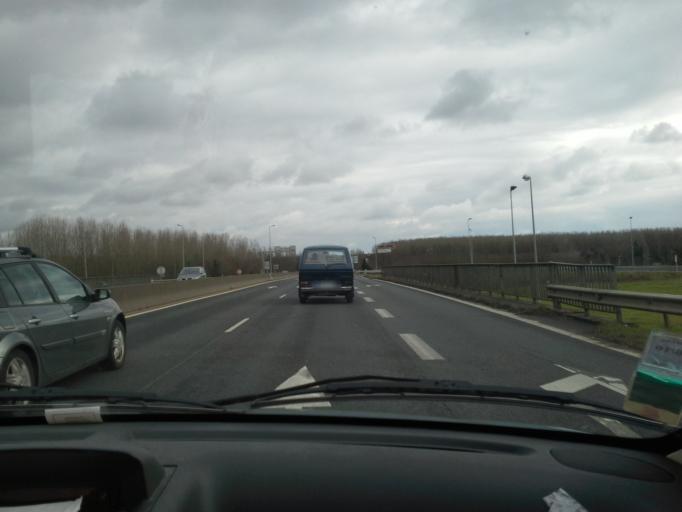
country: FR
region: Centre
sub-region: Departement du Loir-et-Cher
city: Vineuil
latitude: 47.5914
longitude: 1.3572
